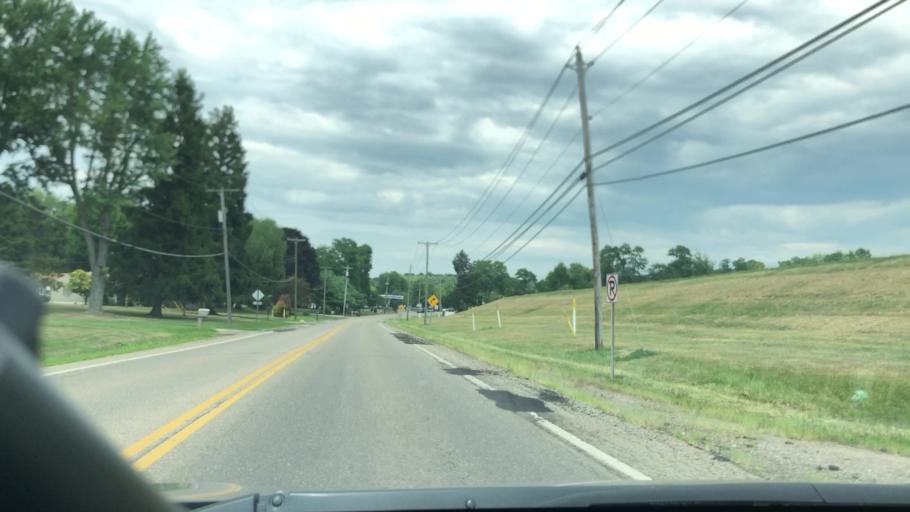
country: US
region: Ohio
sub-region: Summit County
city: New Franklin
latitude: 40.9545
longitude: -81.5329
